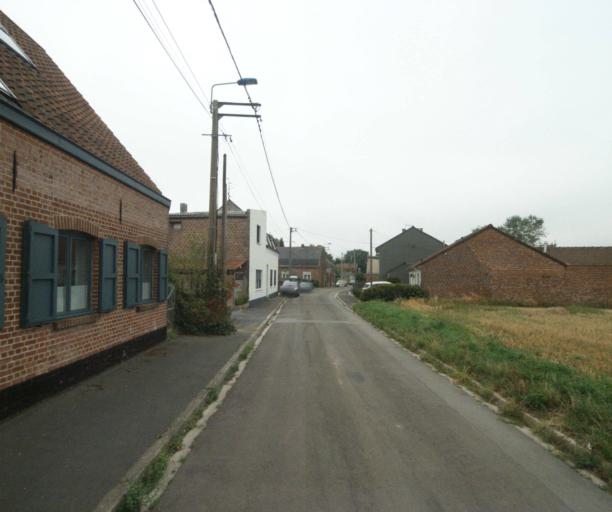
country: FR
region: Nord-Pas-de-Calais
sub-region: Departement du Nord
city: Willems
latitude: 50.6371
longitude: 3.2408
